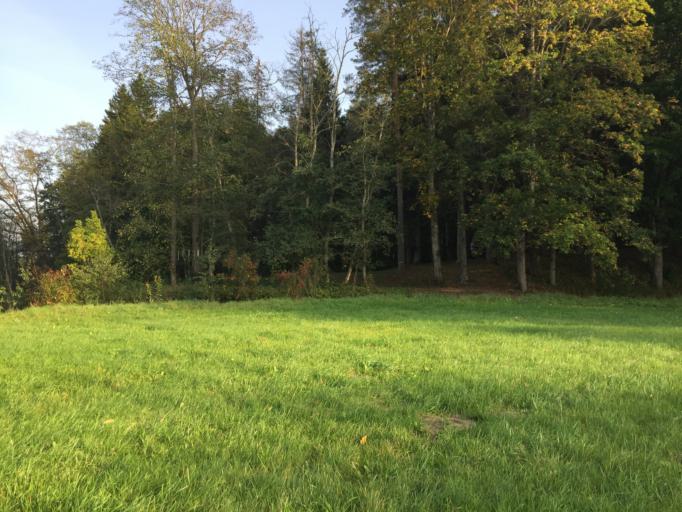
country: LV
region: Garkalne
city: Garkalne
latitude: 56.9688
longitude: 24.4947
